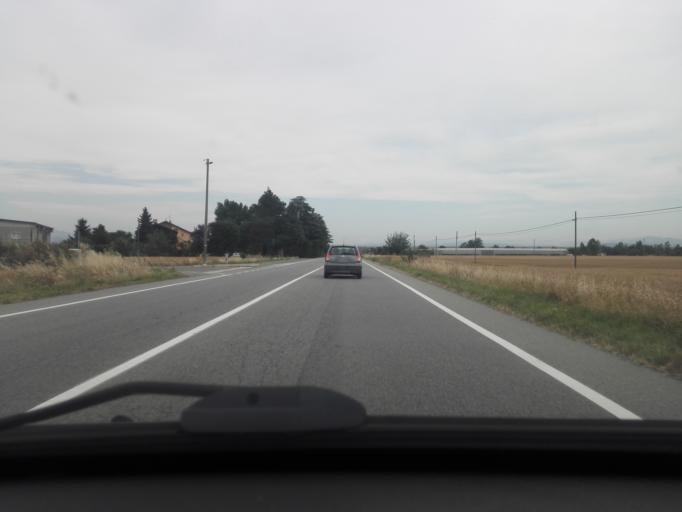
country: IT
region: Piedmont
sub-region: Provincia di Alessandria
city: Pozzolo Formigaro
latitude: 44.8134
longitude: 8.7612
